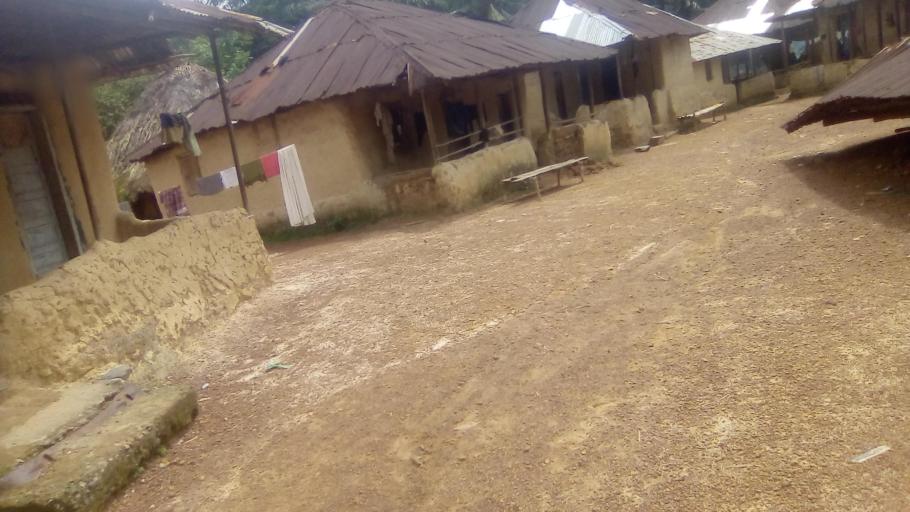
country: SL
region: Southern Province
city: Moyamba
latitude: 8.1382
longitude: -12.4043
